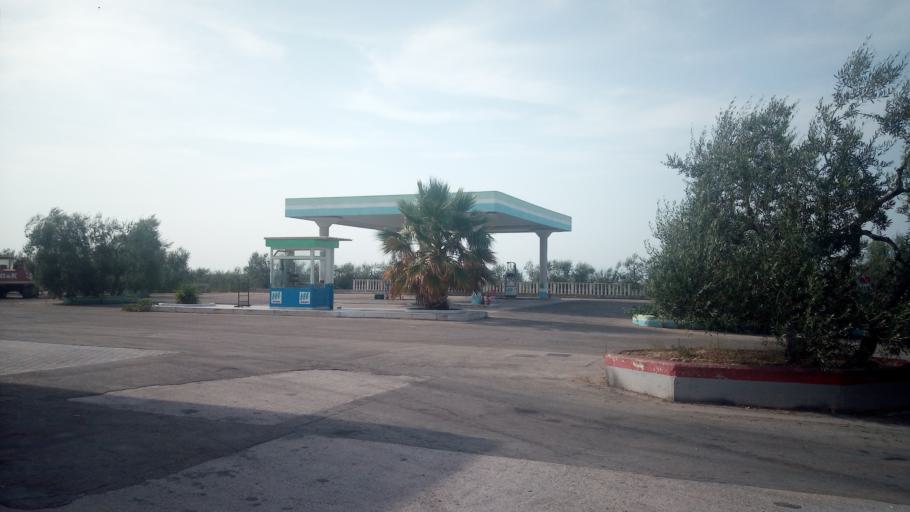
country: IT
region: Apulia
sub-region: Provincia di Barletta - Andria - Trani
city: San Ferdinando di Puglia
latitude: 41.3121
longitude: 16.0844
